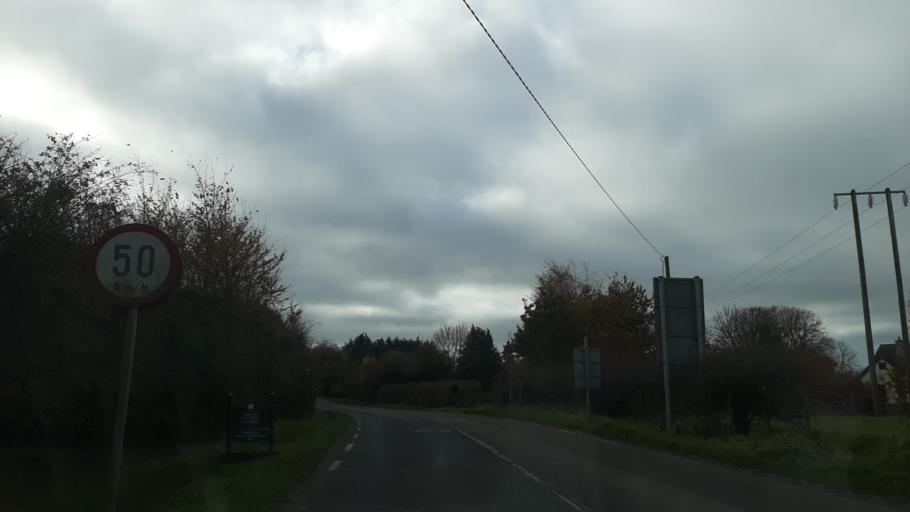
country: IE
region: Leinster
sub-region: Kildare
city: Kildare
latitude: 53.1723
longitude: -6.9003
